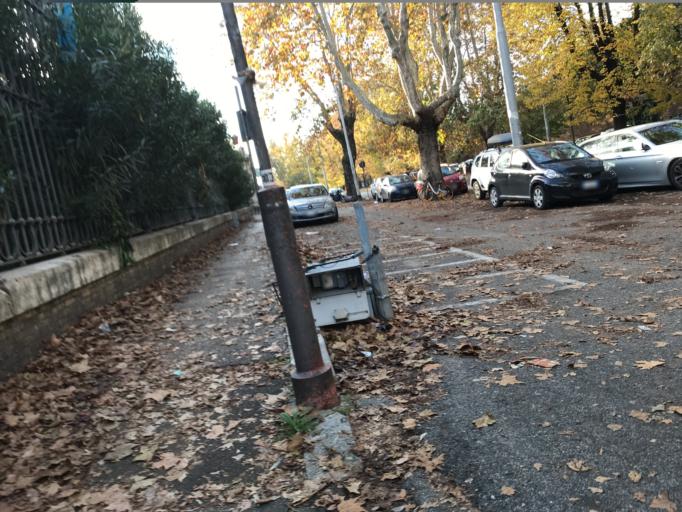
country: IT
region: Latium
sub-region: Citta metropolitana di Roma Capitale
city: Rome
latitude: 41.9067
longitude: 12.5096
